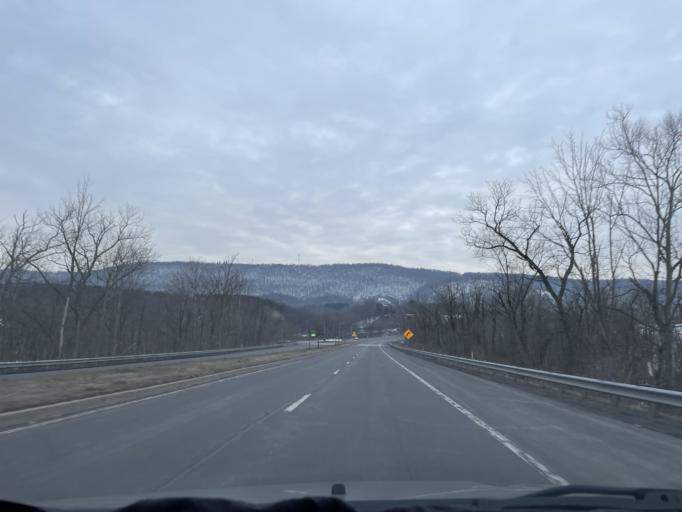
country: US
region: Maryland
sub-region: Allegany County
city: Cumberland
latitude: 39.6279
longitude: -78.7403
